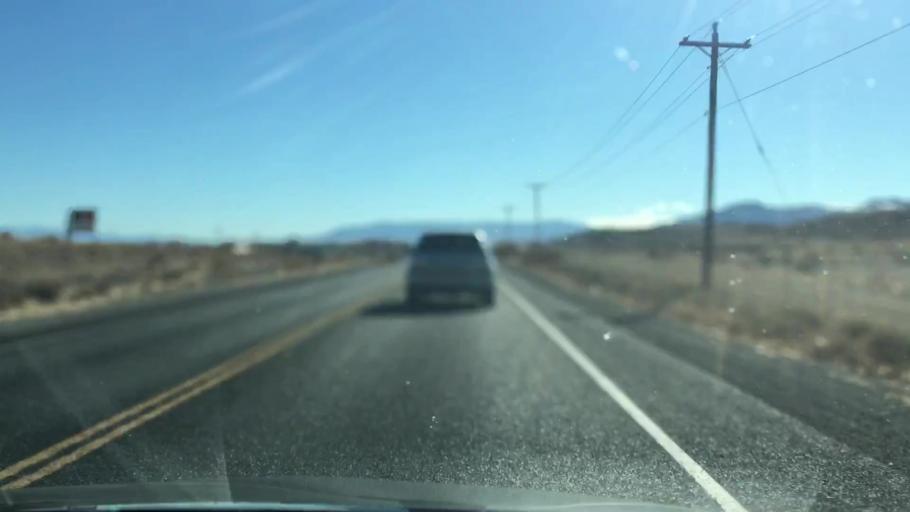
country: US
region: Nevada
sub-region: Lyon County
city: Yerington
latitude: 39.0086
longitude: -119.1828
